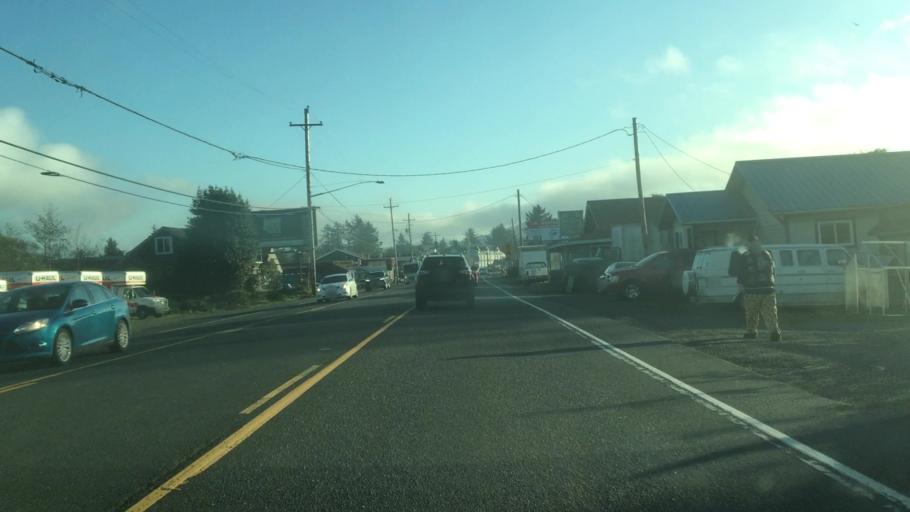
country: US
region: Oregon
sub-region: Clatsop County
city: Seaside
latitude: 45.9809
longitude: -123.9265
